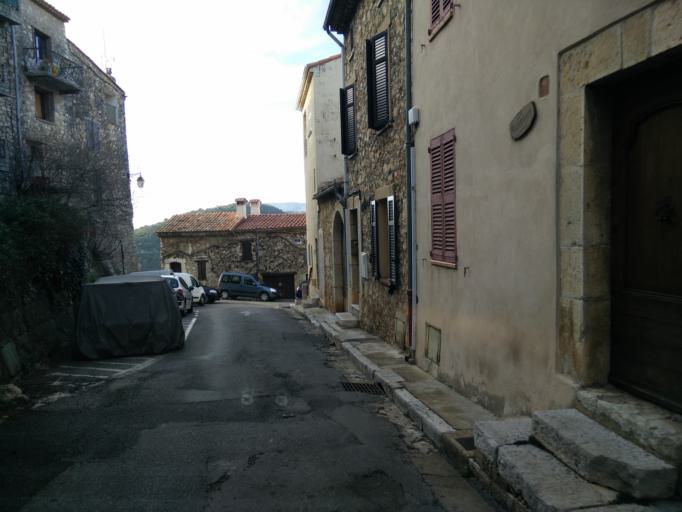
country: FR
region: Provence-Alpes-Cote d'Azur
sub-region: Departement des Alpes-Maritimes
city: Saint-Cezaire-sur-Siagne
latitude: 43.6506
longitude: 6.7918
